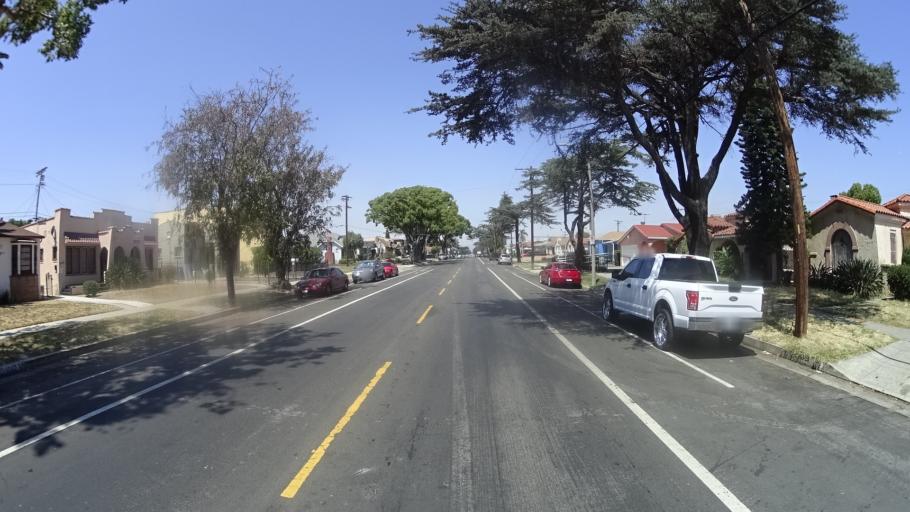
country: US
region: California
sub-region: Los Angeles County
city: Westmont
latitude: 33.9637
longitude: -118.2932
